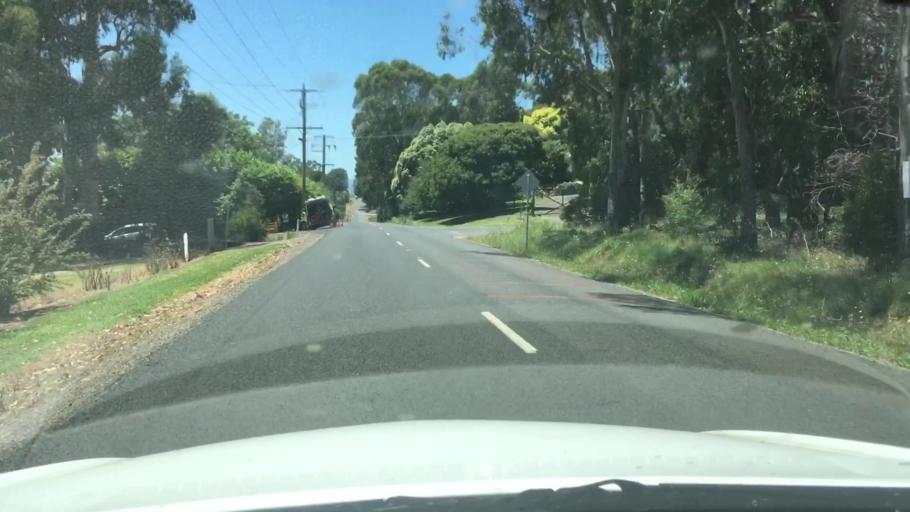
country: AU
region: Victoria
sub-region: Yarra Ranges
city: Mount Evelyn
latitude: -37.8015
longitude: 145.4448
